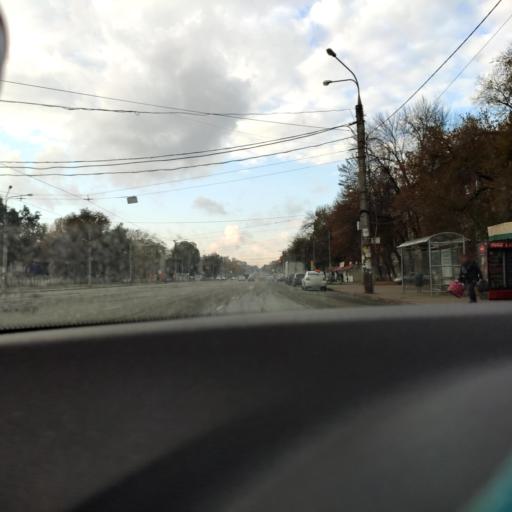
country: RU
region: Samara
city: Samara
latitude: 53.2040
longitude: 50.2388
